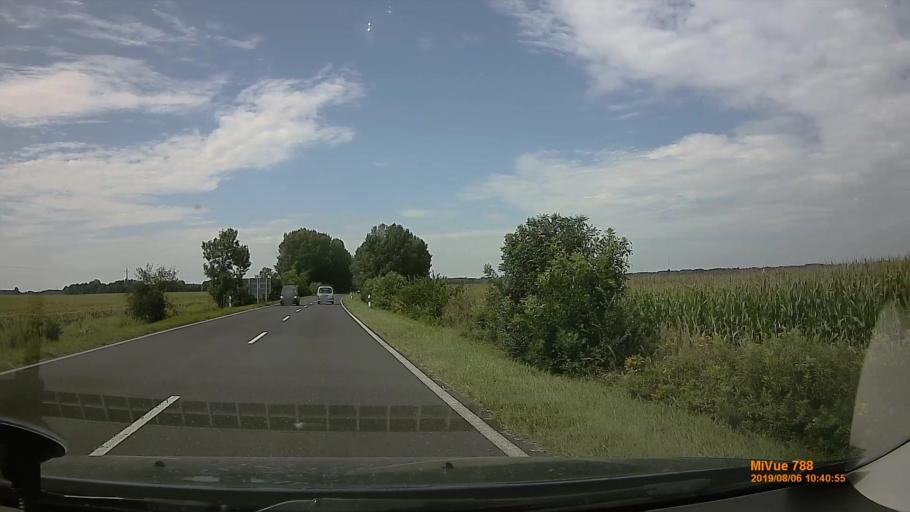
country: HU
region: Zala
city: Zalakomar
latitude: 46.5201
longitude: 17.1463
